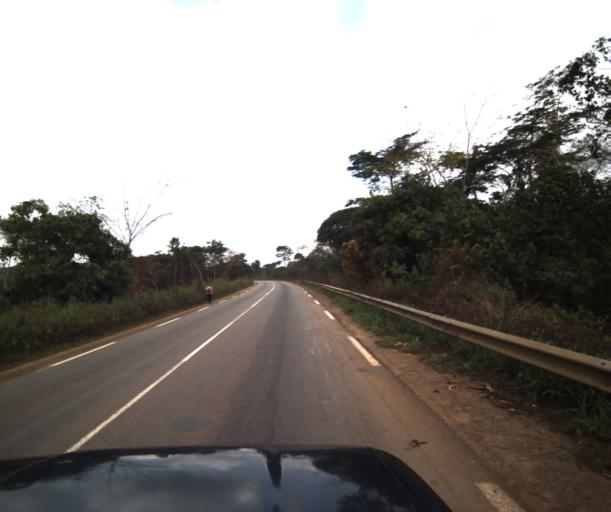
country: CM
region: Centre
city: Mbankomo
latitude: 3.7915
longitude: 11.3072
